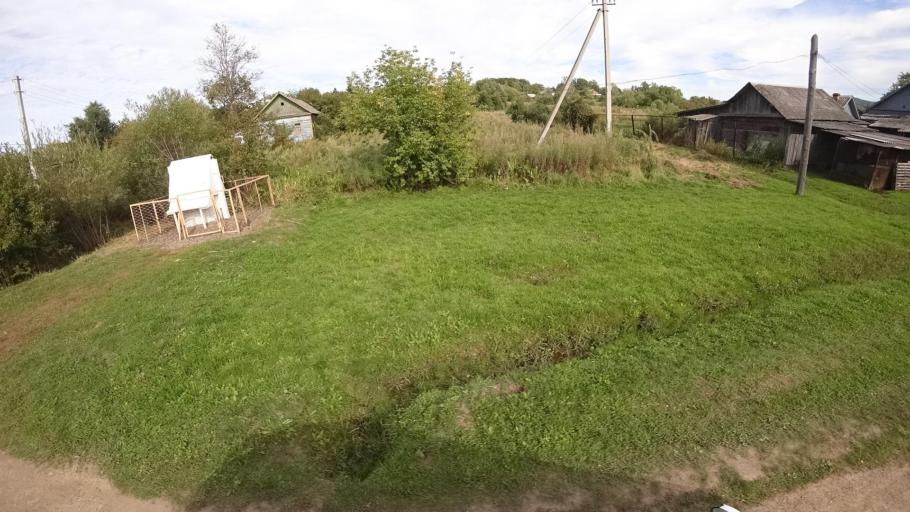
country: RU
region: Primorskiy
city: Dostoyevka
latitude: 44.3208
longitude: 133.4761
